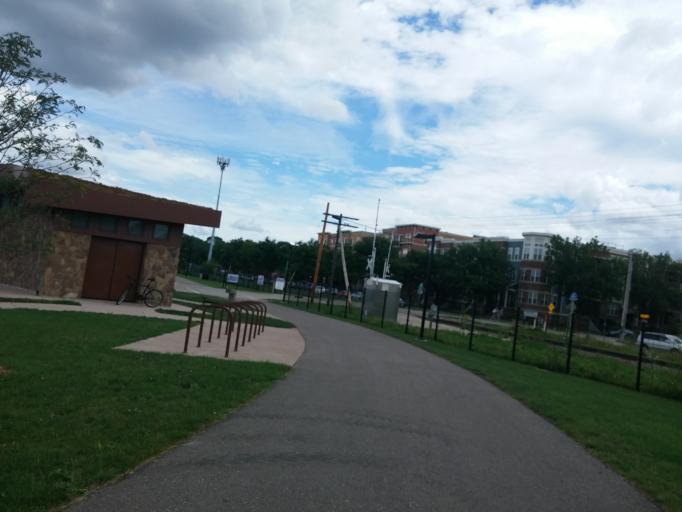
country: US
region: Wisconsin
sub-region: Dane County
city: Madison
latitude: 43.0828
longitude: -89.3678
